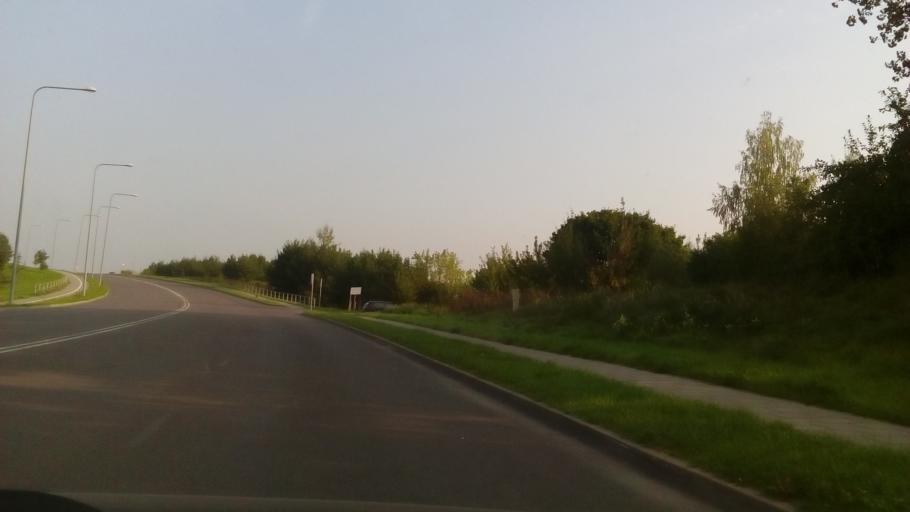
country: LT
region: Alytaus apskritis
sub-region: Alytus
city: Alytus
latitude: 54.4004
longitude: 24.0155
